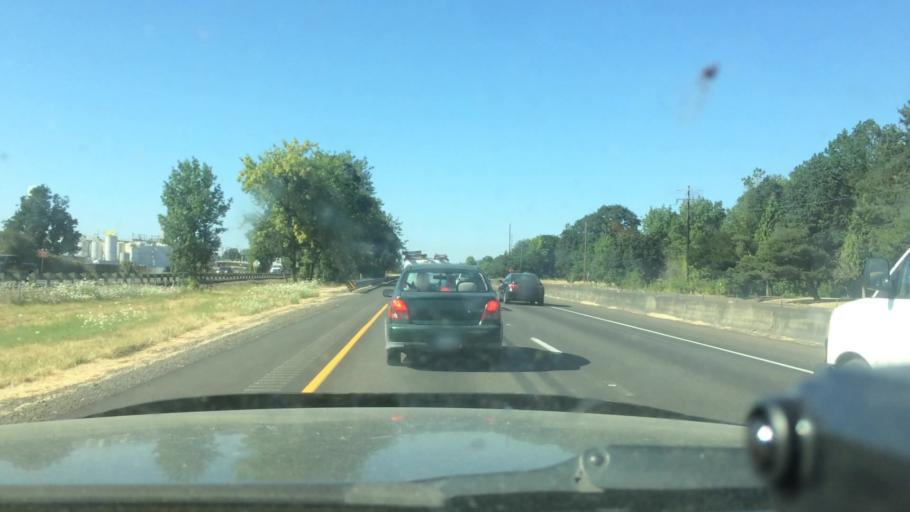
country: US
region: Oregon
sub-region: Linn County
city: Millersburg
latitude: 44.6603
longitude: -123.0598
